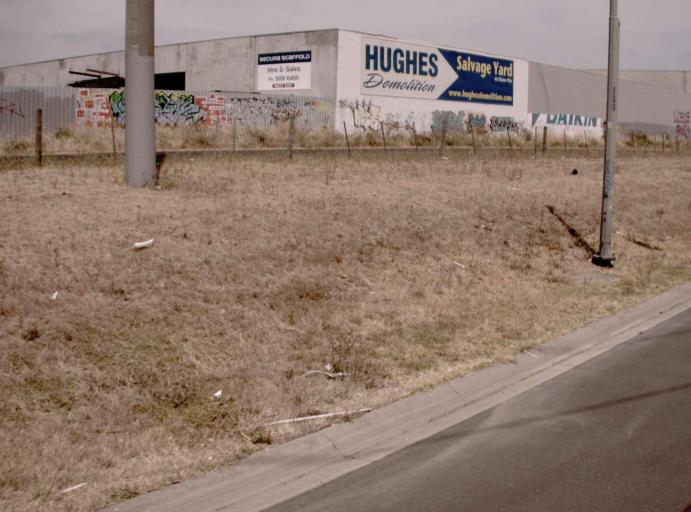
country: AU
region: Victoria
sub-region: Moonee Valley
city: Keilor East
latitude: -37.7338
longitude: 144.8535
